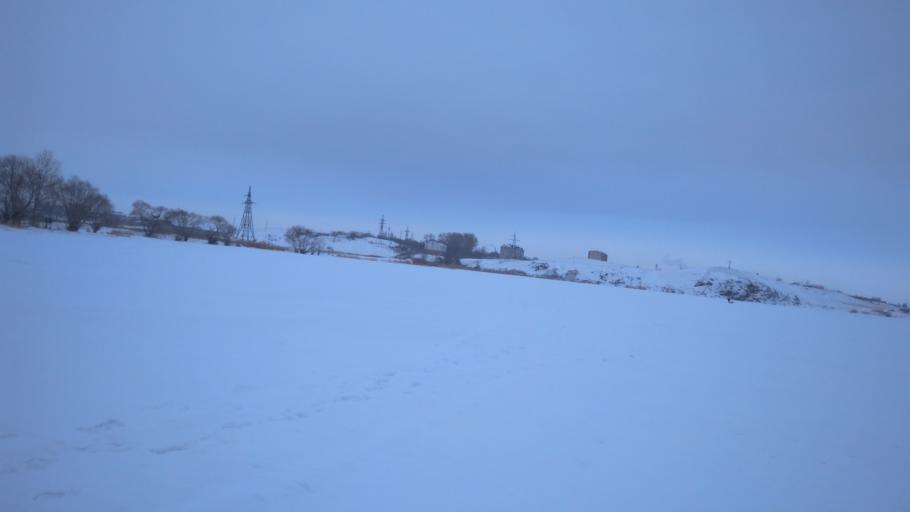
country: RU
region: Chelyabinsk
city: Troitsk
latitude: 54.0820
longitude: 61.5725
